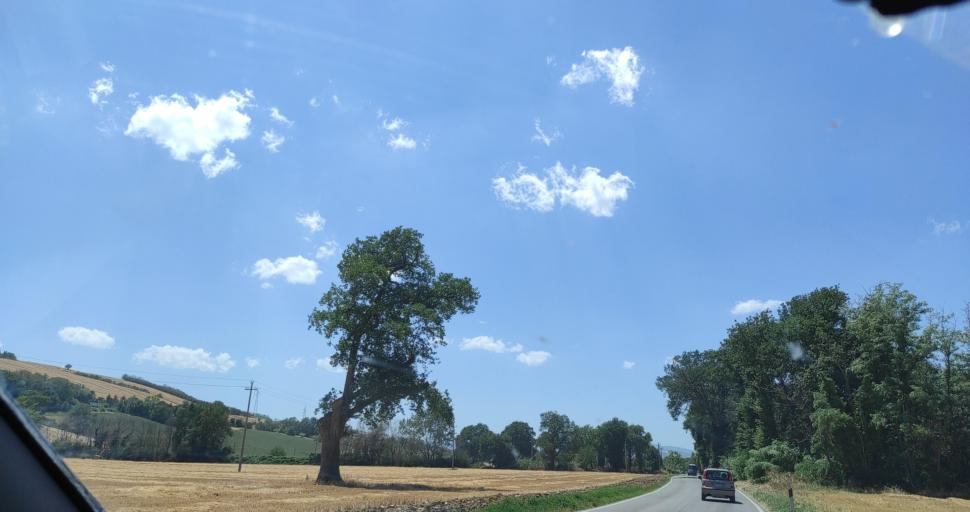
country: IT
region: The Marches
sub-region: Provincia di Macerata
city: Casette Verdini
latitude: 43.2324
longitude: 13.3767
